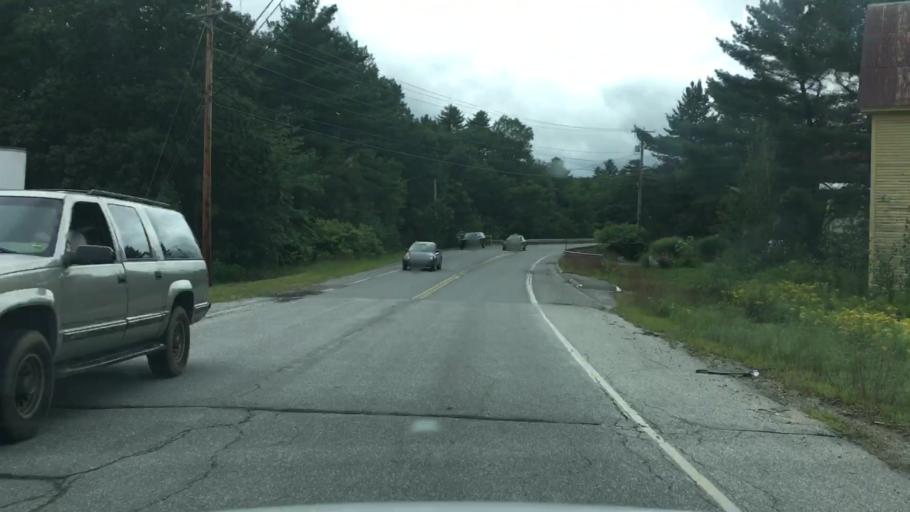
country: US
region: Maine
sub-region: York County
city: Cornish
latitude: 43.8081
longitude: -70.7790
